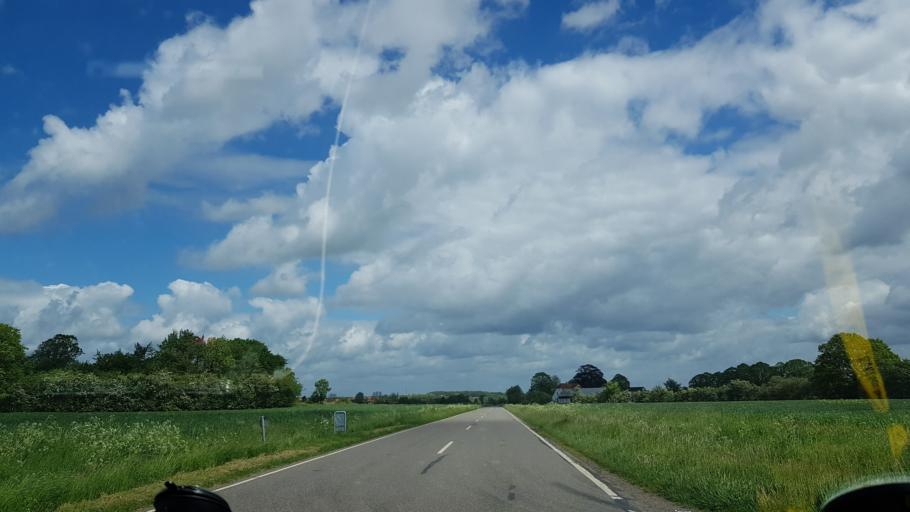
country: DK
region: South Denmark
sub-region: Kolding Kommune
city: Christiansfeld
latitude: 55.3404
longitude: 9.4650
